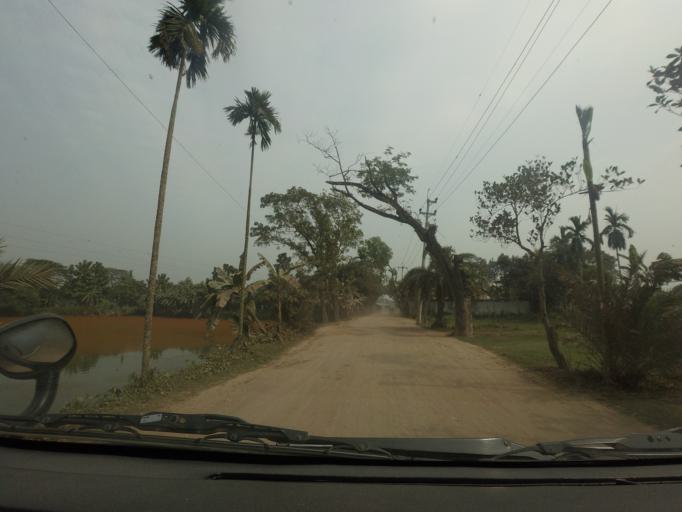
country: BD
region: Dhaka
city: Kishorganj
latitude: 24.3428
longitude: 90.7908
